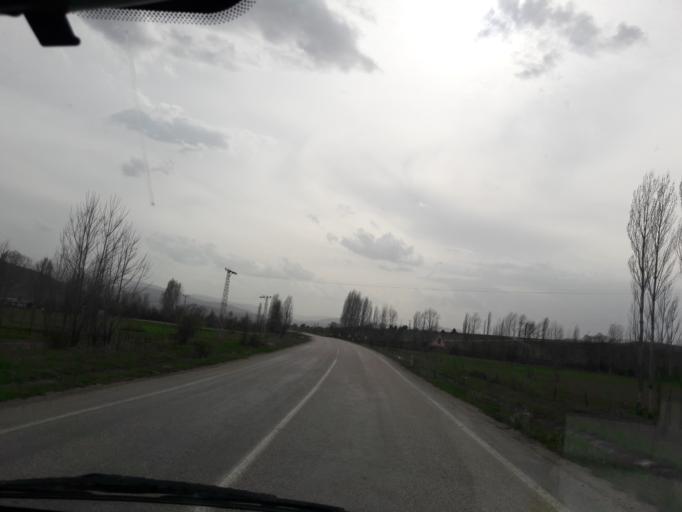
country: TR
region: Gumushane
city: Siran
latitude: 40.1770
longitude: 39.0925
